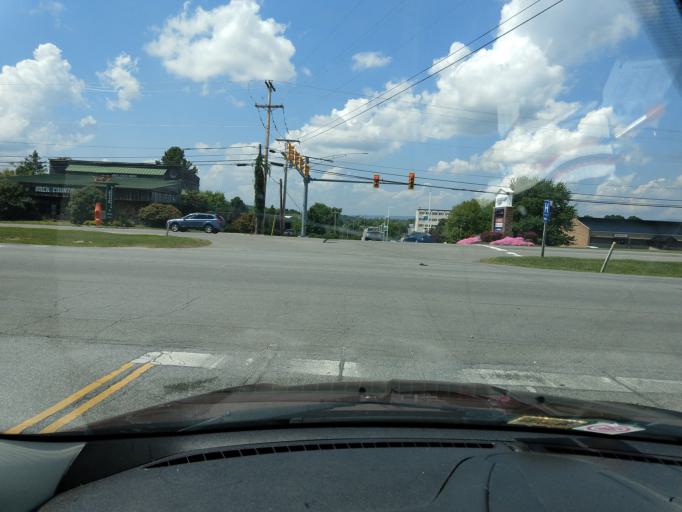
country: US
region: Virginia
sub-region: Montgomery County
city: Merrimac
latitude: 37.1854
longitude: -80.4083
